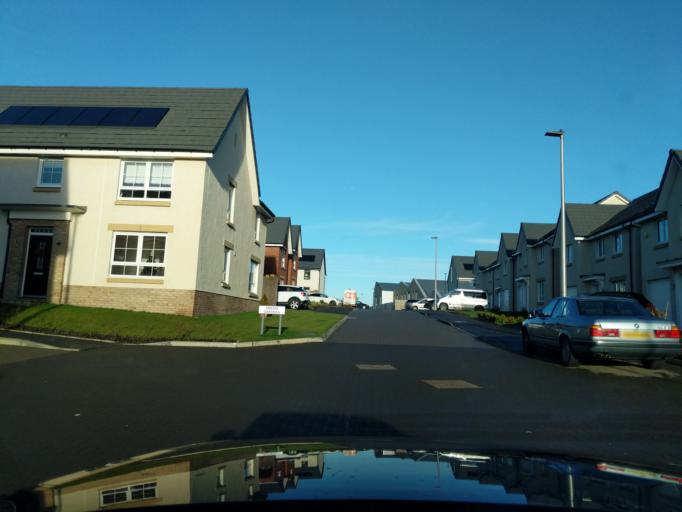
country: GB
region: Scotland
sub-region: Midlothian
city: Loanhead
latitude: 55.8972
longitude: -3.1638
